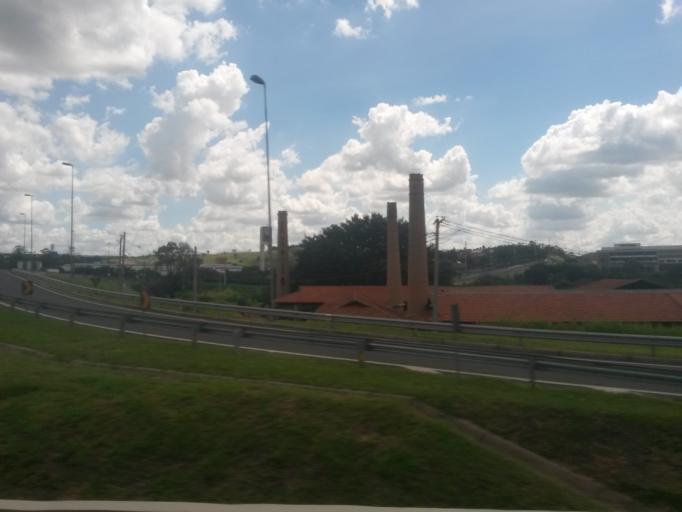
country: BR
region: Sao Paulo
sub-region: Vinhedo
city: Vinhedo
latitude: -23.0600
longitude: -46.9948
